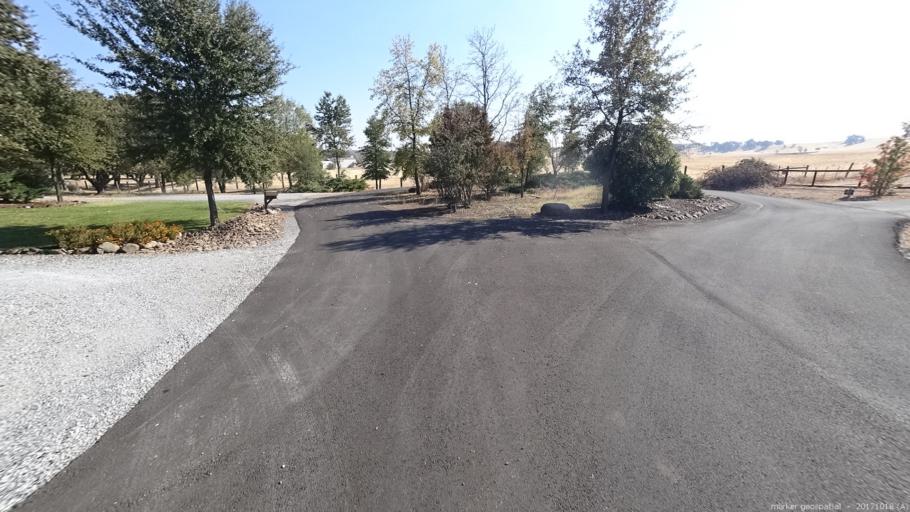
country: US
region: California
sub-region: Shasta County
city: Palo Cedro
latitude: 40.5403
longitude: -122.1695
